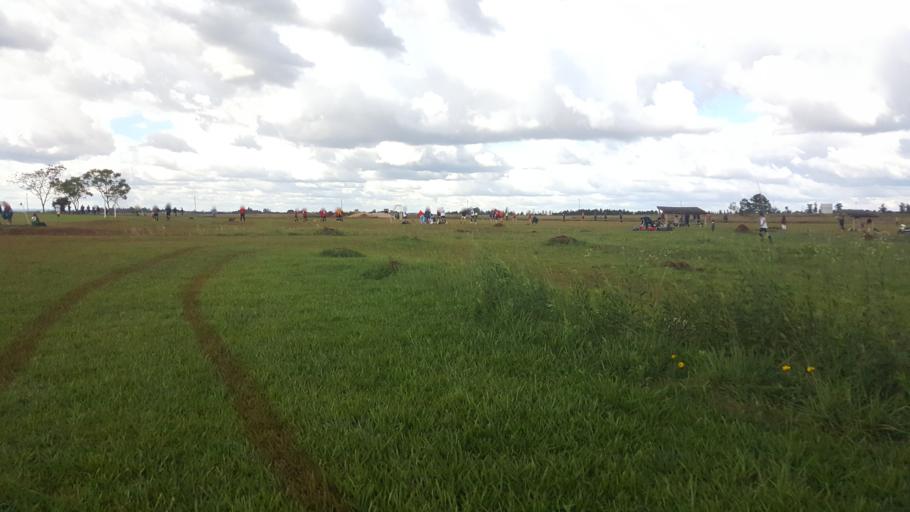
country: AR
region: Misiones
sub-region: Departamento de Capital
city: Posadas
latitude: -27.4159
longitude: -56.0067
